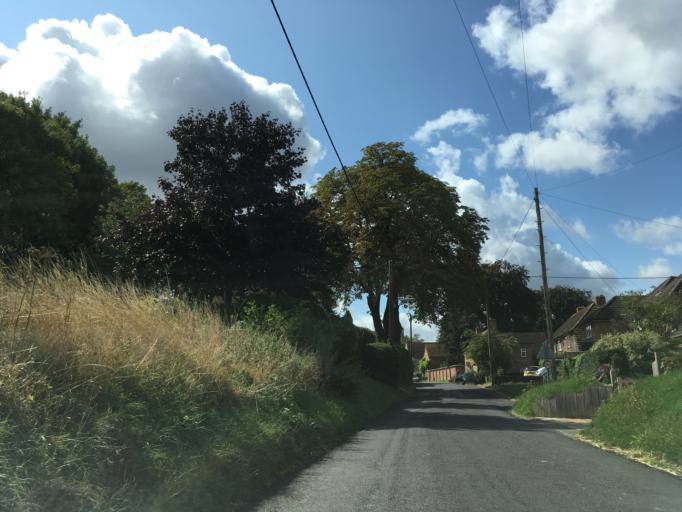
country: GB
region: England
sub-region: Hampshire
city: Kings Worthy
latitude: 51.1693
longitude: -1.3783
